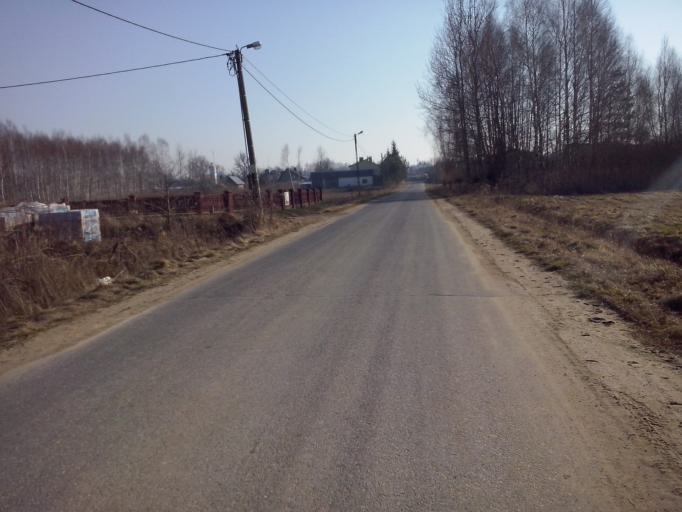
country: PL
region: Subcarpathian Voivodeship
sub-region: Powiat nizanski
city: Krzeszow
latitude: 50.4186
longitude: 22.3478
